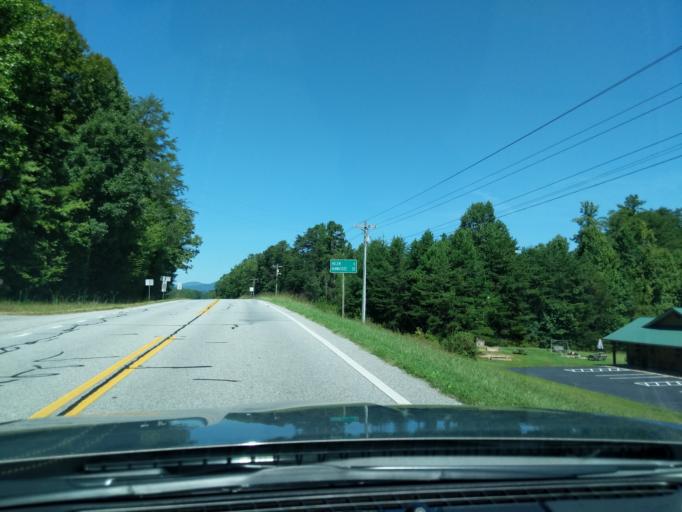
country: US
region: Georgia
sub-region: Habersham County
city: Clarkesville
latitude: 34.6641
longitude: -83.6438
